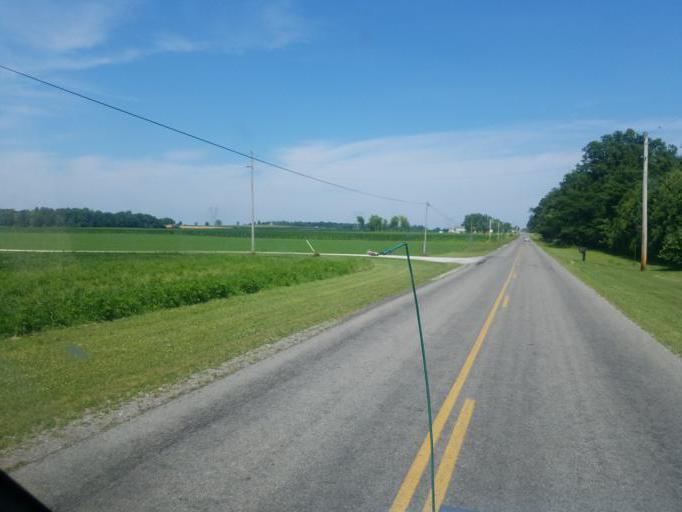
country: US
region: Ohio
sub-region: Shelby County
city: Jackson Center
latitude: 40.4977
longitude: -84.0942
